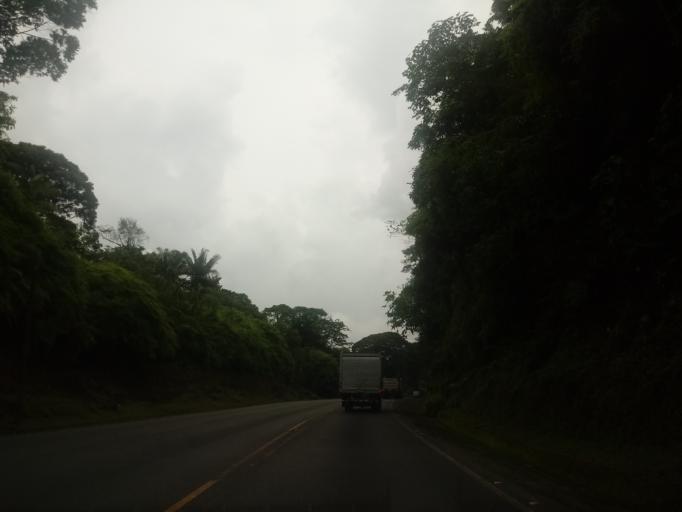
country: CR
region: San Jose
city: Dulce Nombre de Jesus
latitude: 10.1728
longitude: -83.9326
